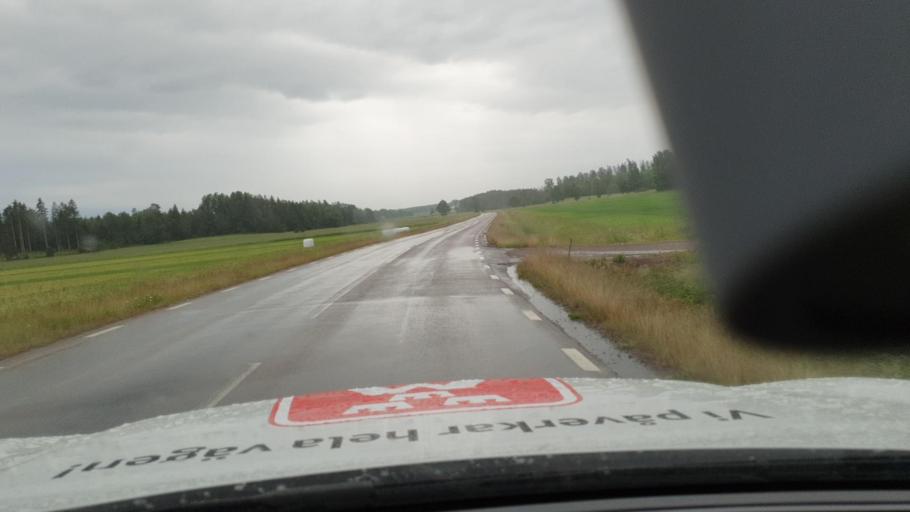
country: SE
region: Vaestra Goetaland
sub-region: Mariestads Kommun
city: Mariestad
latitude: 58.7745
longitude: 13.9070
